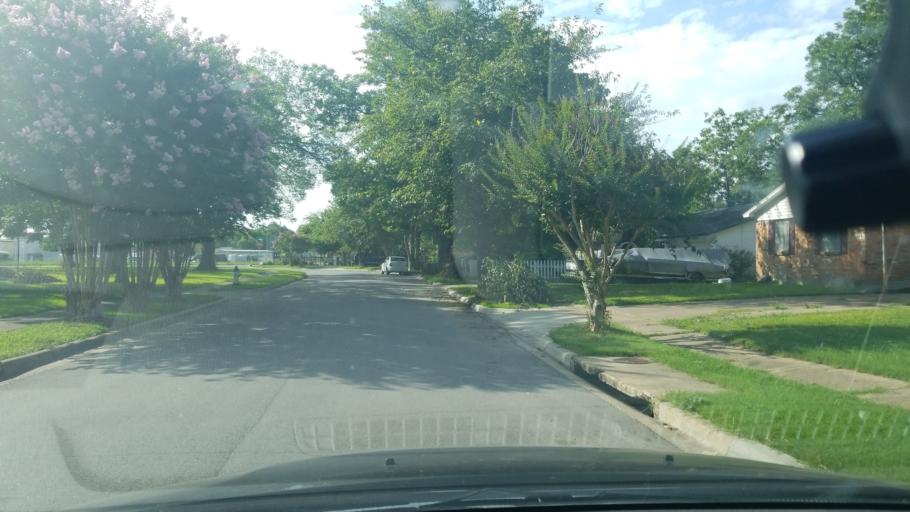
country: US
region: Texas
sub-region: Dallas County
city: Balch Springs
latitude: 32.7455
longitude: -96.6706
